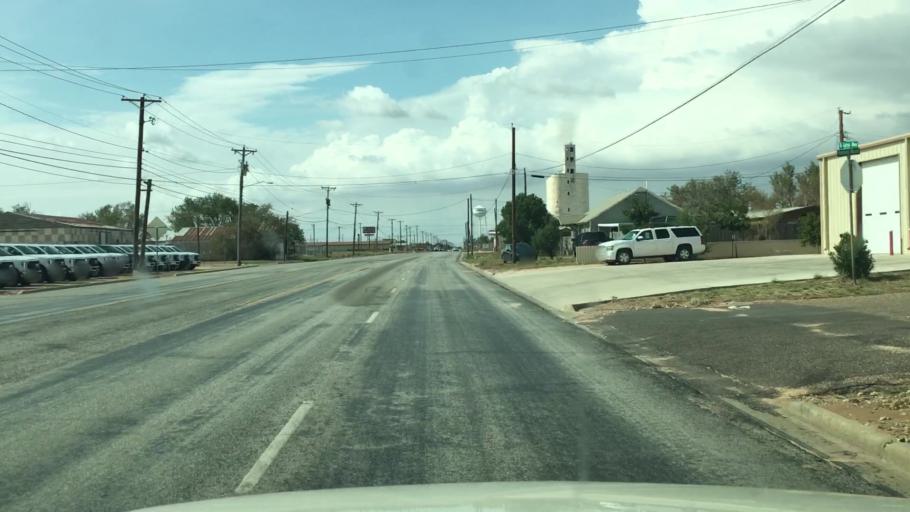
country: US
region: Texas
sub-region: Dawson County
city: Lamesa
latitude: 32.7231
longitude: -101.9461
